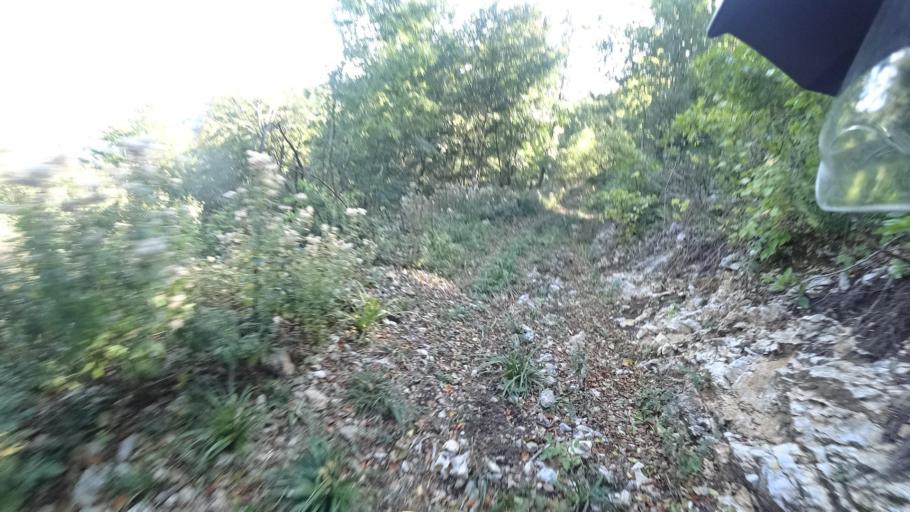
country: HR
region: Primorsko-Goranska
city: Vrbovsko
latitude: 45.2822
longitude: 15.1234
